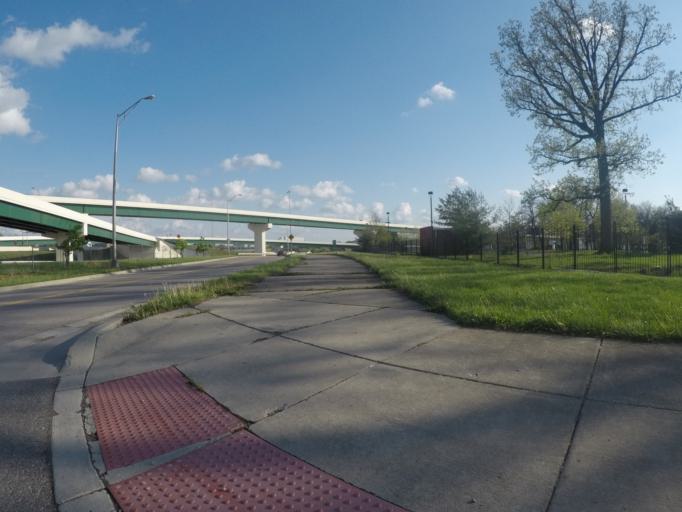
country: US
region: Ohio
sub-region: Franklin County
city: Columbus
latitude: 39.9743
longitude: -82.9845
